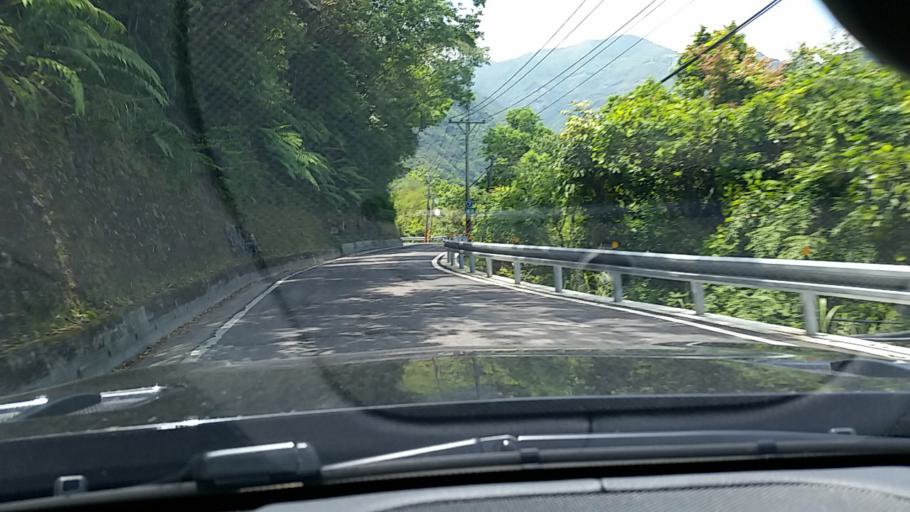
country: TW
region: Taiwan
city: Daxi
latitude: 24.6991
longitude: 121.3719
